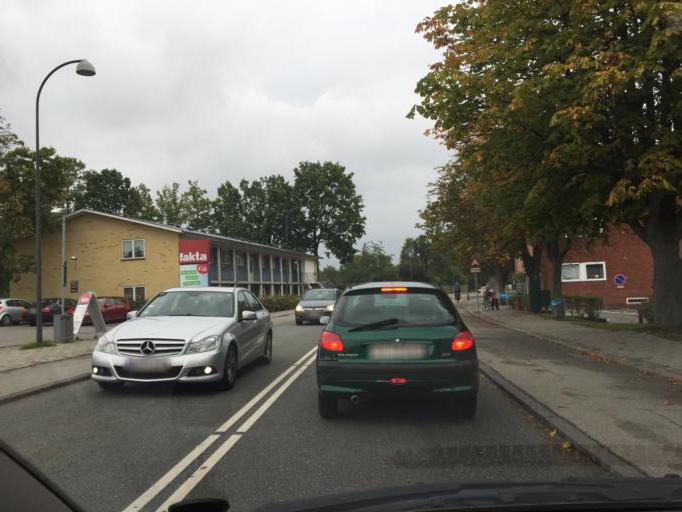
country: DK
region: Capital Region
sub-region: Herlev Kommune
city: Herlev
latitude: 55.7275
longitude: 12.4321
